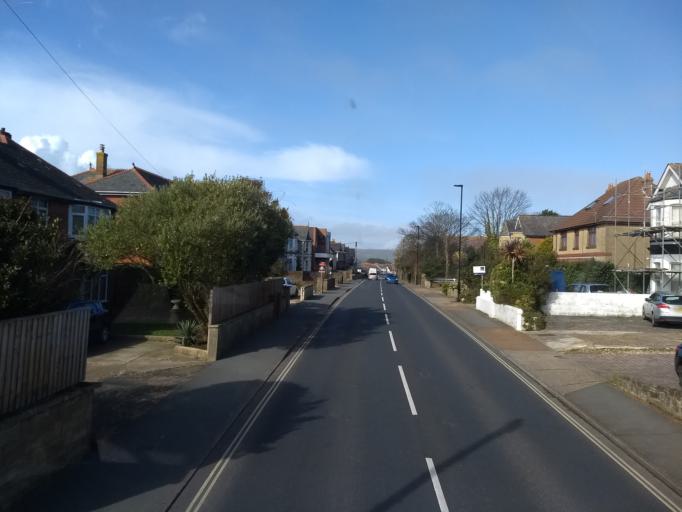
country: GB
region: England
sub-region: Isle of Wight
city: Sandown
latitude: 50.6453
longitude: -1.1687
